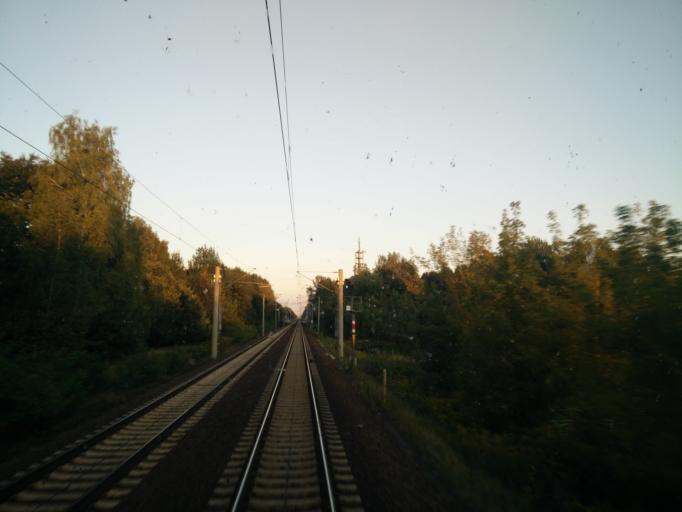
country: DE
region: Brandenburg
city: Dallgow-Doeberitz
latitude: 52.5710
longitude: 13.0461
